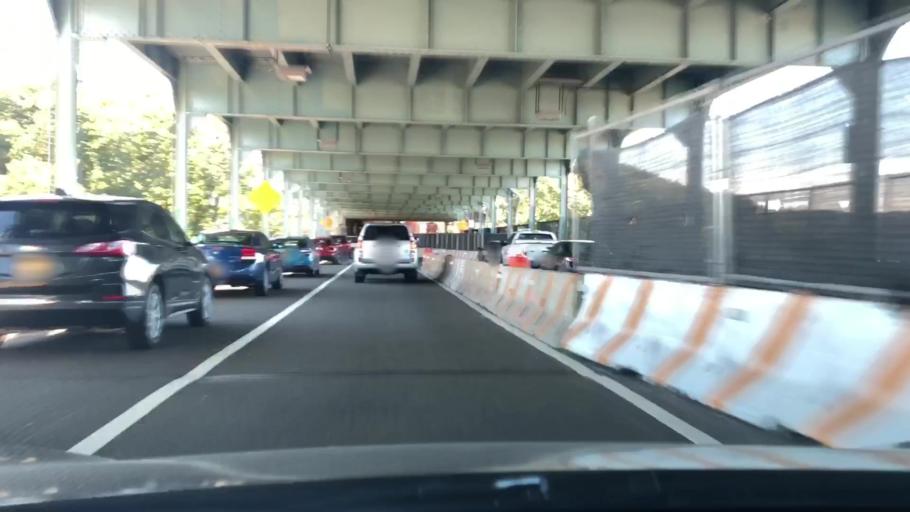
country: US
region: New York
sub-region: New York County
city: Inwood
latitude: 40.8775
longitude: -73.9227
